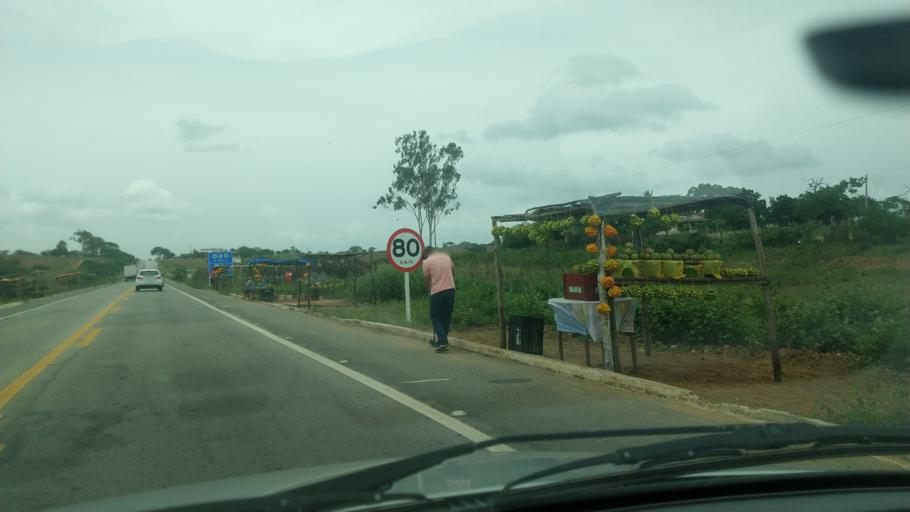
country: BR
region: Rio Grande do Norte
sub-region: Santa Cruz
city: Santa Cruz
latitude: -6.2111
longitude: -36.1818
